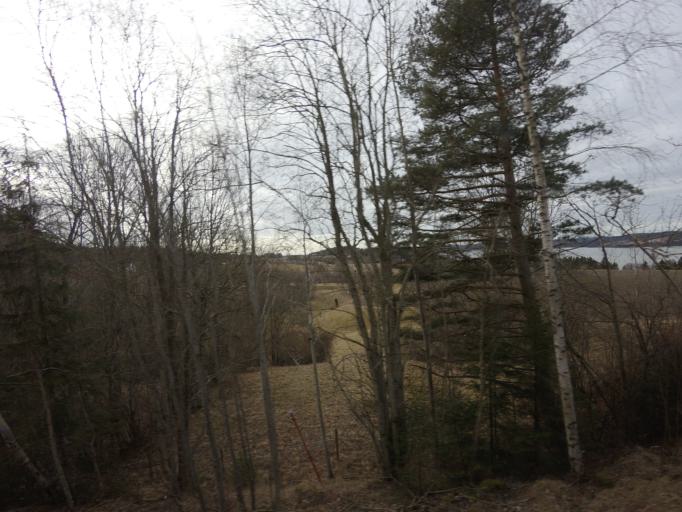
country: NO
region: Akershus
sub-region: Enebakk
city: Flateby
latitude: 59.8060
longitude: 11.2546
